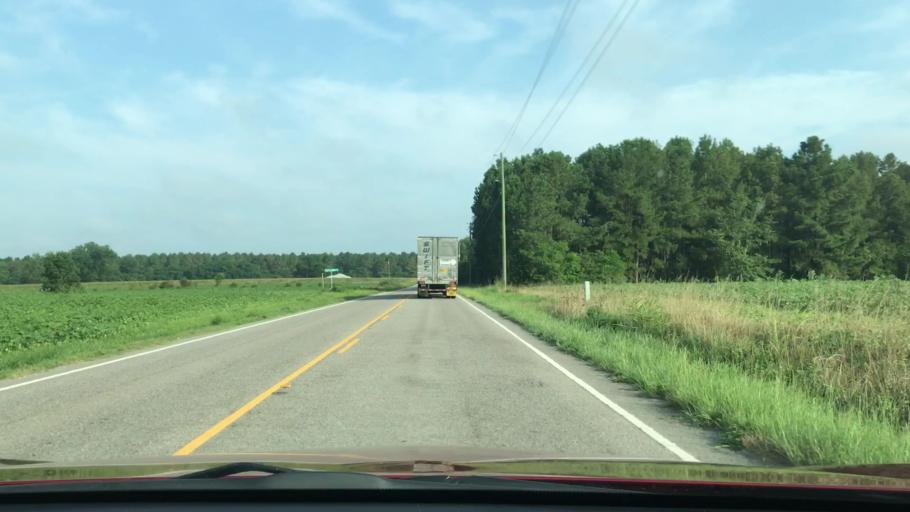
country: US
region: South Carolina
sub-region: Barnwell County
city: Blackville
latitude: 33.5978
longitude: -81.2592
